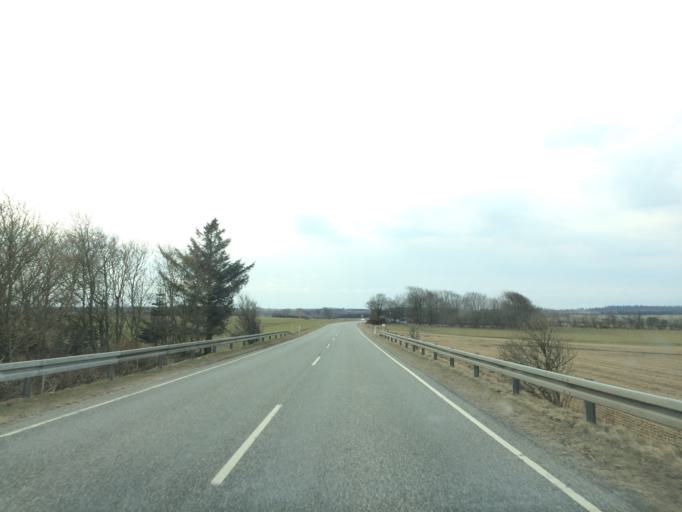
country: DK
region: Central Jutland
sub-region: Ringkobing-Skjern Kommune
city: Videbaek
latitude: 56.0771
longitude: 8.5070
